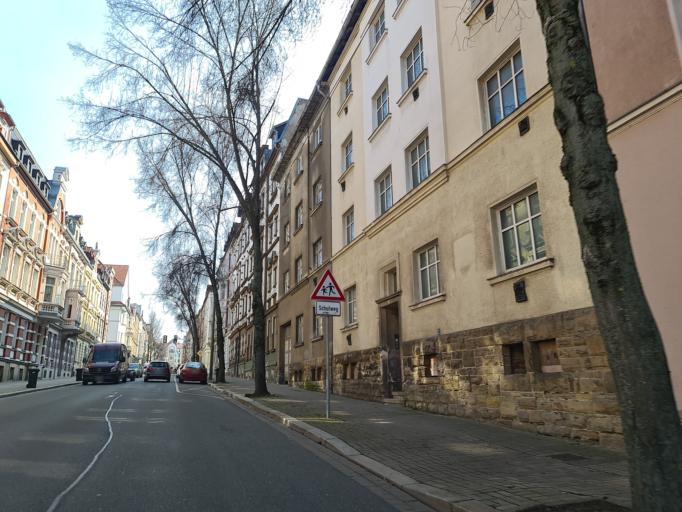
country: DE
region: Saxony-Anhalt
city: Zeitz
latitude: 51.0474
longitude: 12.1435
